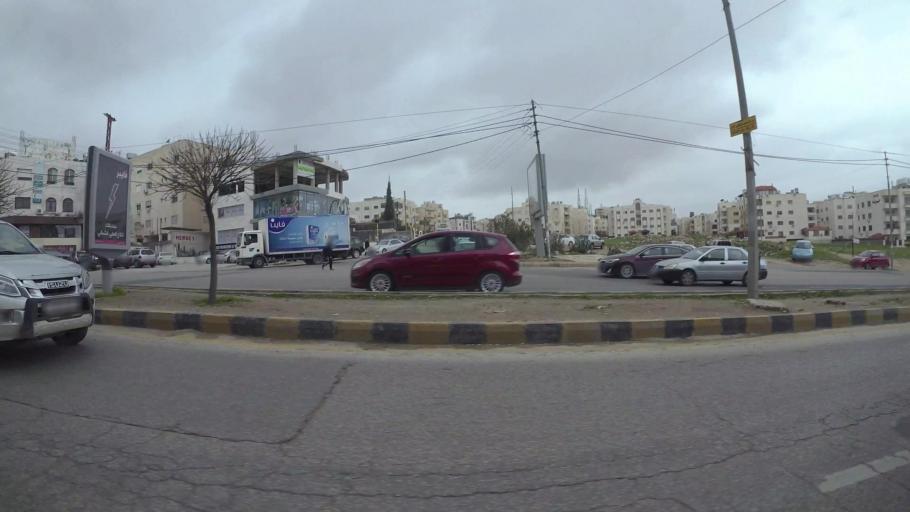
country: JO
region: Amman
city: Al Jubayhah
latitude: 31.9970
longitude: 35.8429
